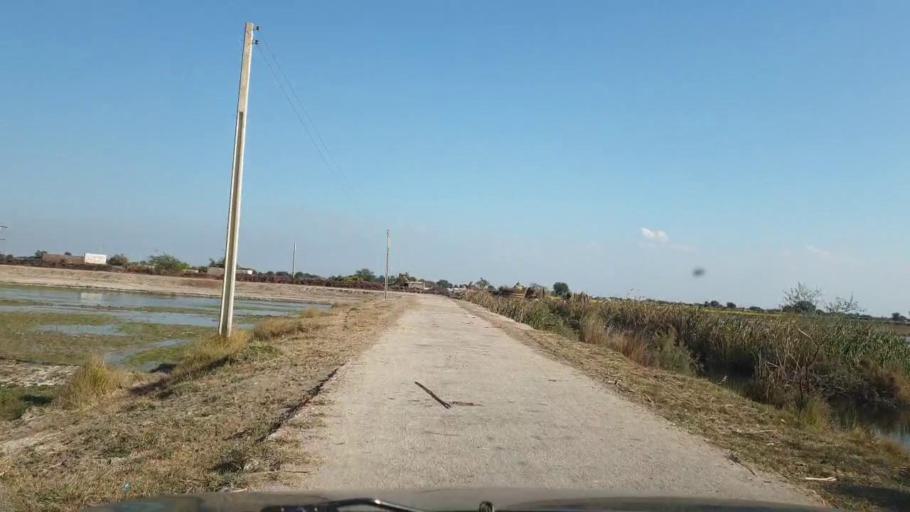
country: PK
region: Sindh
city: Sinjhoro
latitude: 25.9745
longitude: 68.7283
